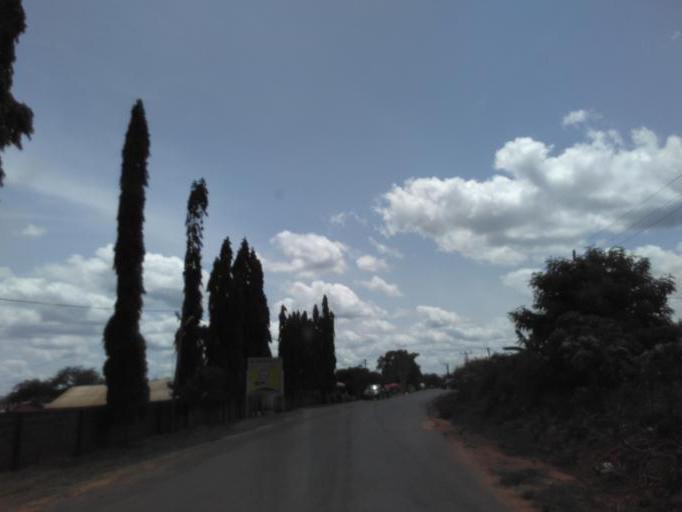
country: GH
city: Akropong
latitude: 6.0833
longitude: -0.0997
